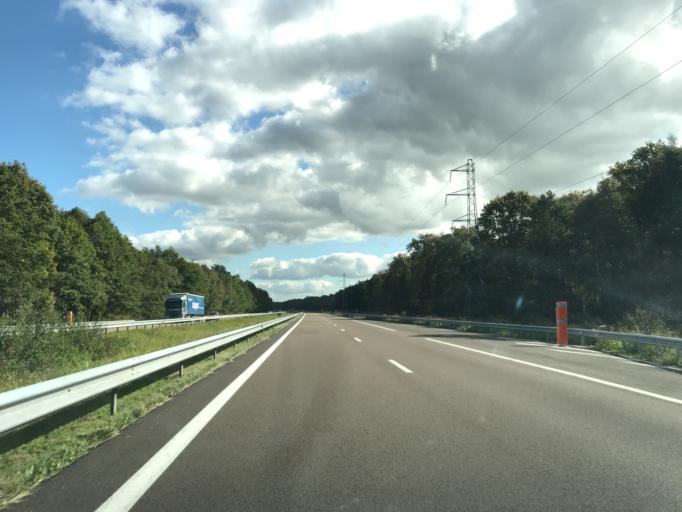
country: FR
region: Centre
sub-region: Departement du Loiret
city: Courtenay
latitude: 48.0936
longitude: 3.0344
